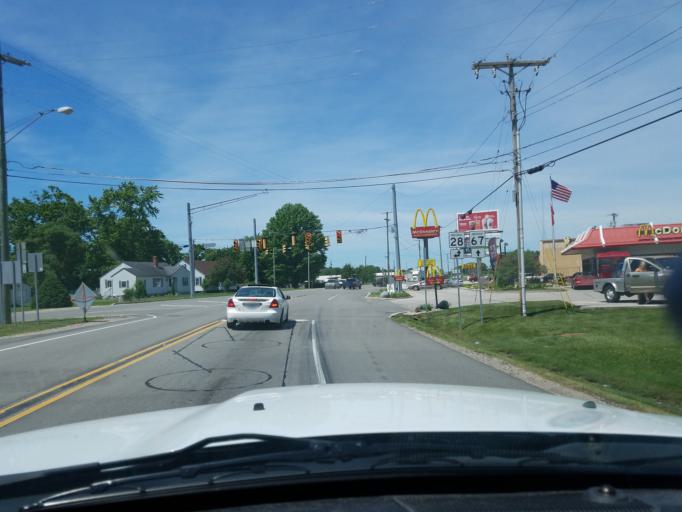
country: US
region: Indiana
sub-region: Delaware County
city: Albany
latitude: 40.2999
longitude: -85.2490
